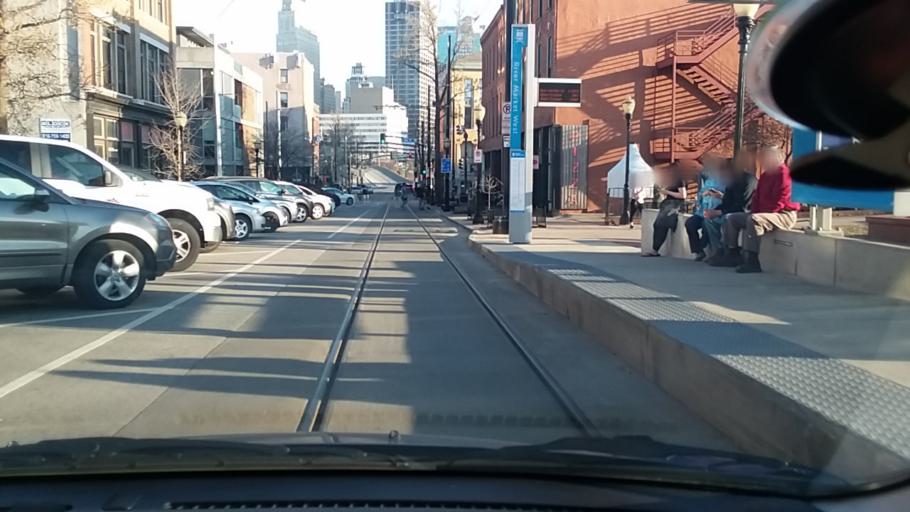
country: US
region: Missouri
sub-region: Jackson County
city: Kansas City
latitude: 39.1088
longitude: -94.5844
